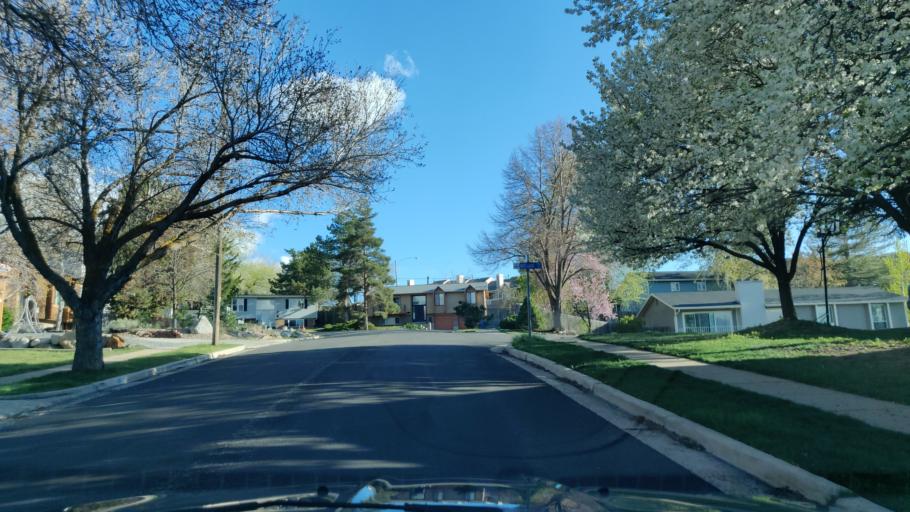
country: US
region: Utah
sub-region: Salt Lake County
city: Little Cottonwood Creek Valley
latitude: 40.6149
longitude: -111.8301
